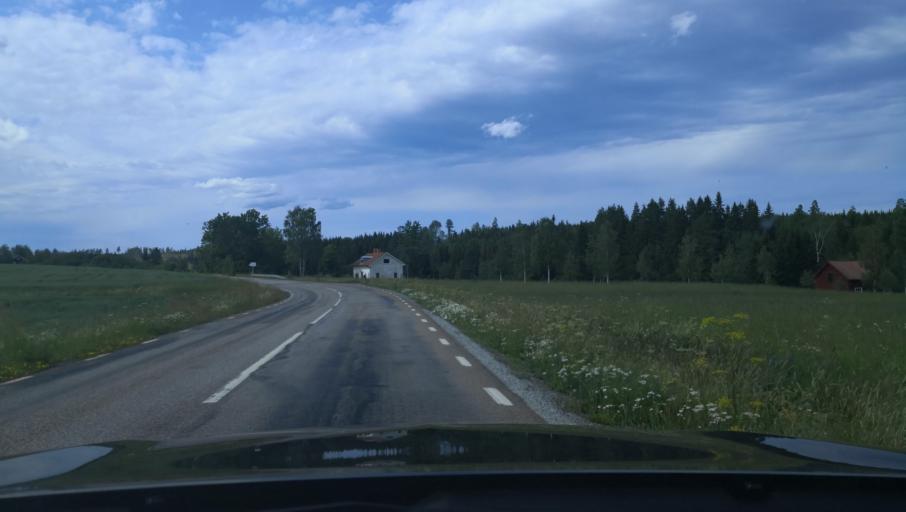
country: SE
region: Dalarna
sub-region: Avesta Kommun
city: Avesta
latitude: 59.9898
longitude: 16.1151
